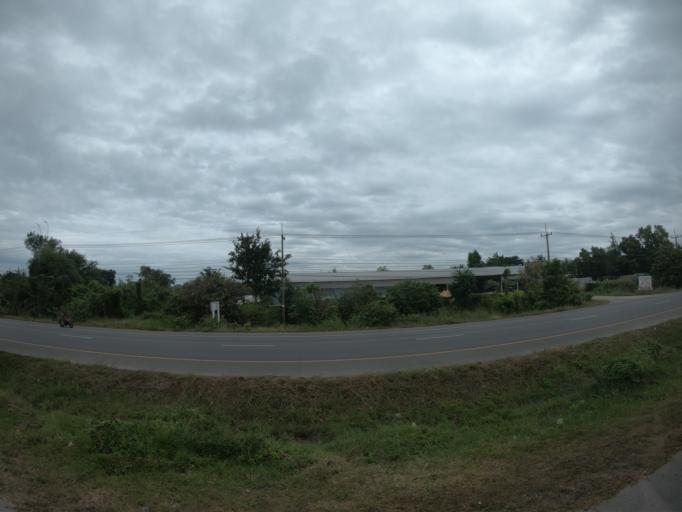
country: TH
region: Maha Sarakham
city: Maha Sarakham
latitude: 16.1577
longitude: 103.3657
